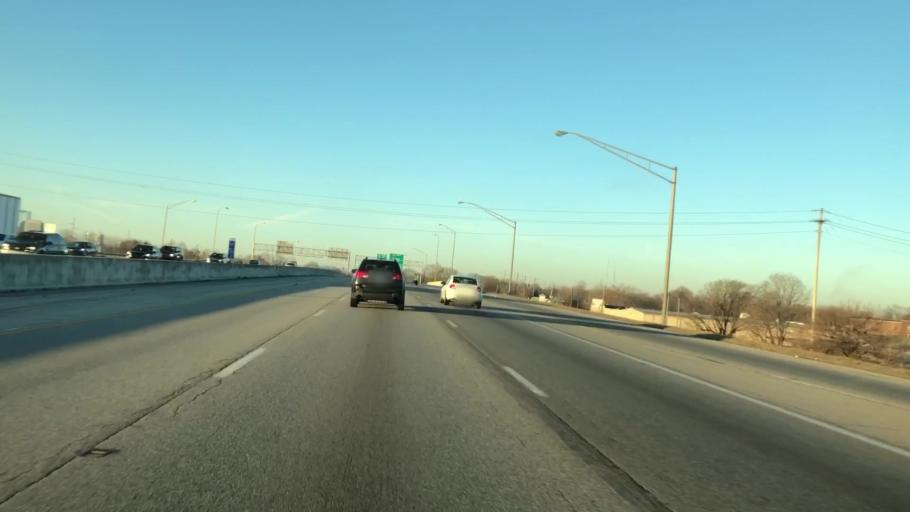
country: US
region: Indiana
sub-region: Marion County
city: Indianapolis
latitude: 39.7396
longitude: -86.1373
